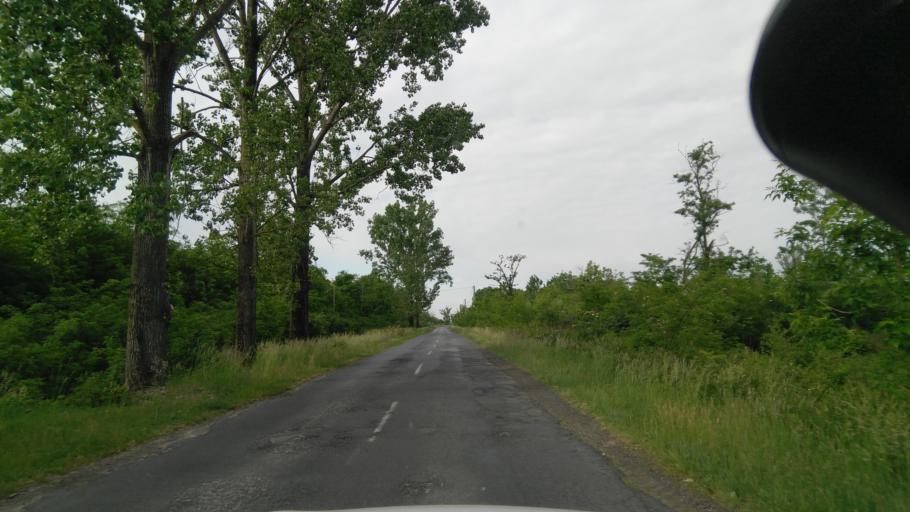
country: HU
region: Bekes
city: Elek
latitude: 46.5901
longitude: 21.2271
